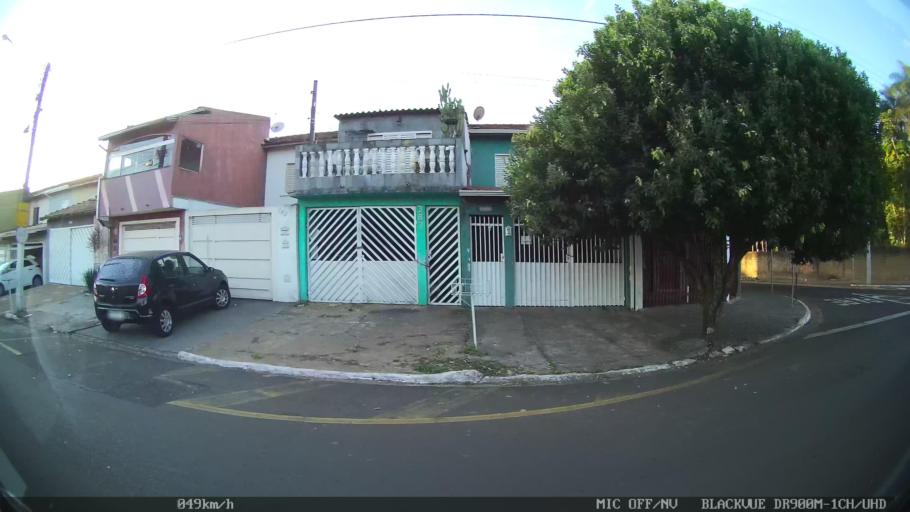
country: BR
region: Sao Paulo
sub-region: Franca
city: Franca
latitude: -20.4929
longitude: -47.4007
